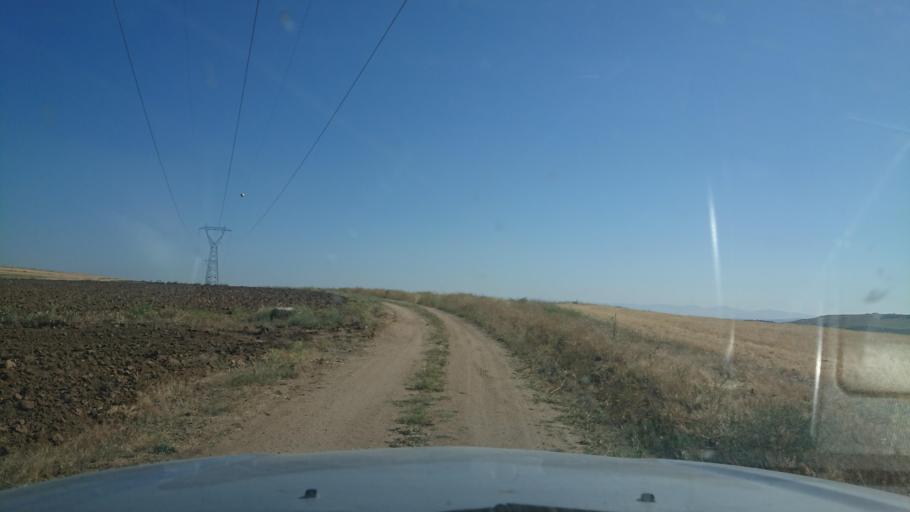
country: TR
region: Aksaray
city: Agacoren
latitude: 38.8346
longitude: 33.9452
